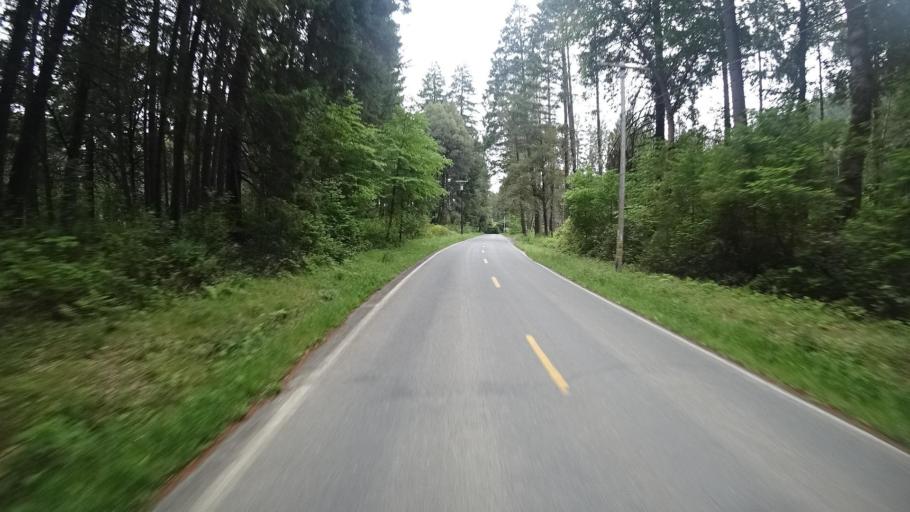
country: US
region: California
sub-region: Humboldt County
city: Willow Creek
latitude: 41.0838
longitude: -123.7042
